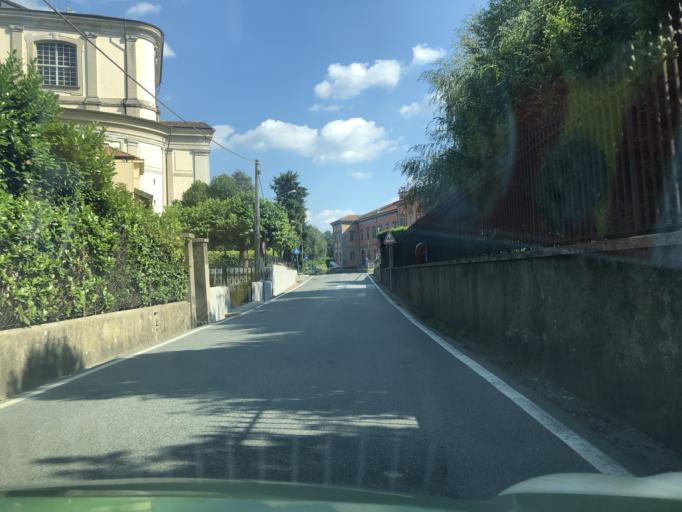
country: IT
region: Piedmont
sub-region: Provincia di Novara
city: Arona
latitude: 45.7702
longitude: 8.5439
